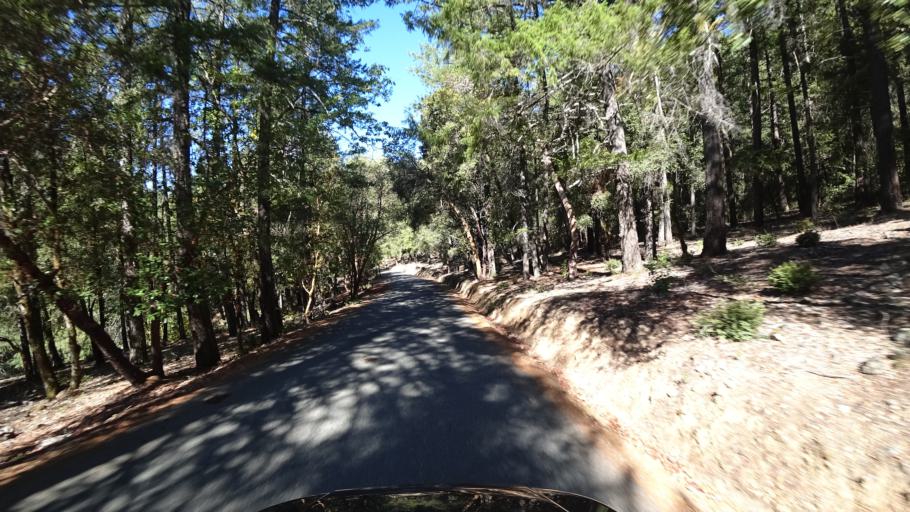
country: US
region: California
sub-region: Humboldt County
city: Willow Creek
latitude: 41.2763
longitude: -123.3437
